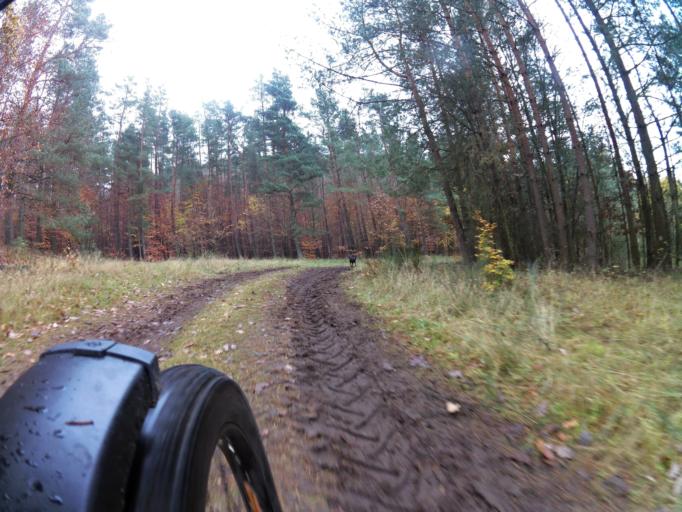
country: PL
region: Pomeranian Voivodeship
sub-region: Powiat pucki
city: Krokowa
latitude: 54.7439
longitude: 18.1011
